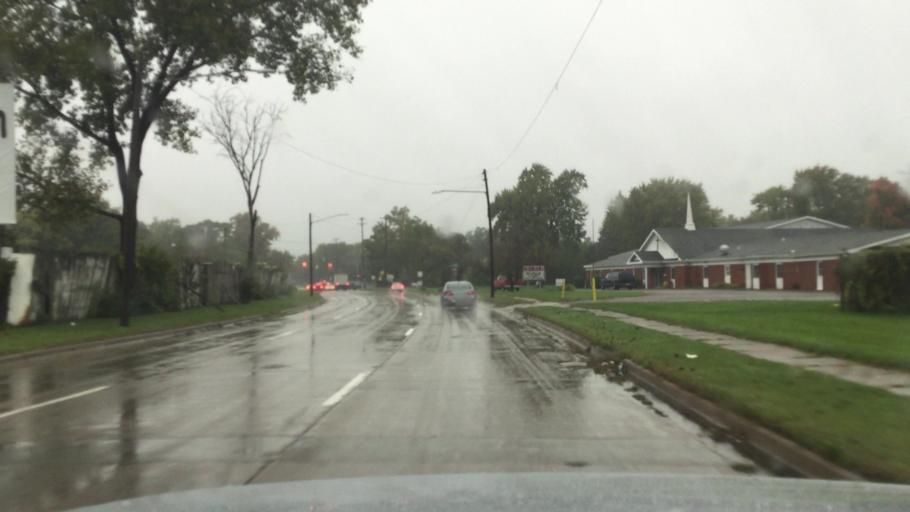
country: US
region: Michigan
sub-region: Saginaw County
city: Buena Vista
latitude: 43.4159
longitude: -83.9196
